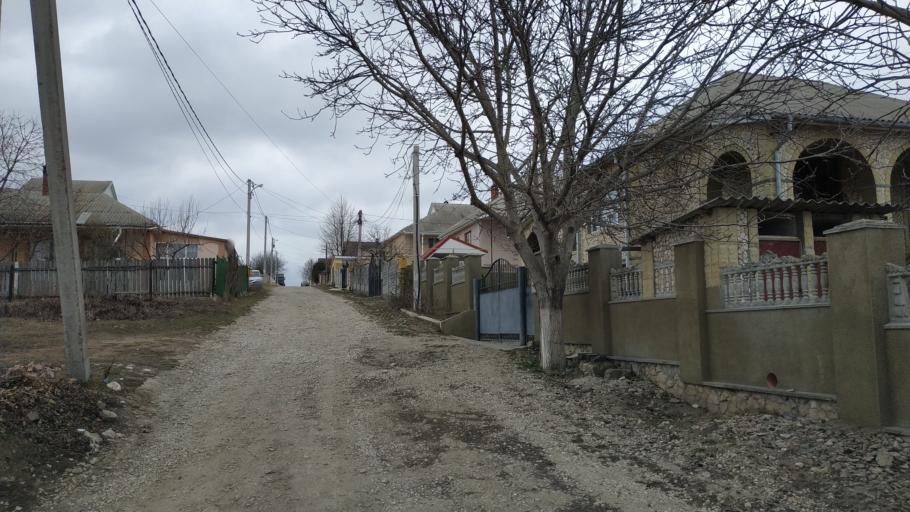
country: MD
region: Laloveni
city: Ialoveni
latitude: 46.9257
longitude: 28.7780
